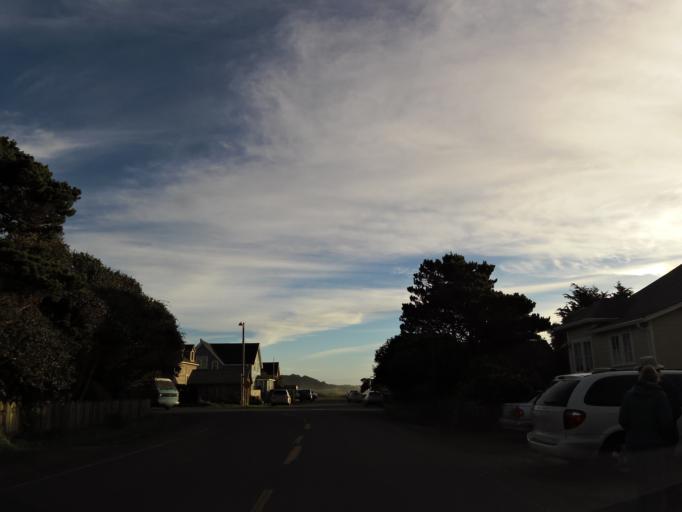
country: US
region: California
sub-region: Mendocino County
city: Fort Bragg
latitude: 39.3055
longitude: -123.8064
